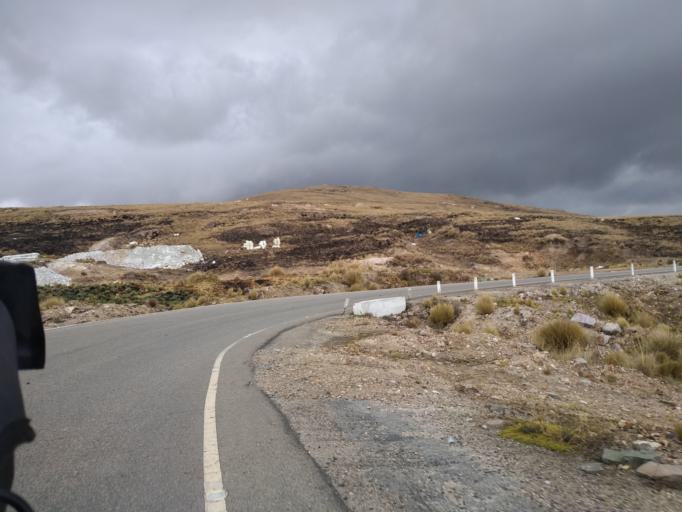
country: PE
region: La Libertad
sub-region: Provincia de Santiago de Chuco
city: Quiruvilca
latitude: -7.9932
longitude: -78.2969
